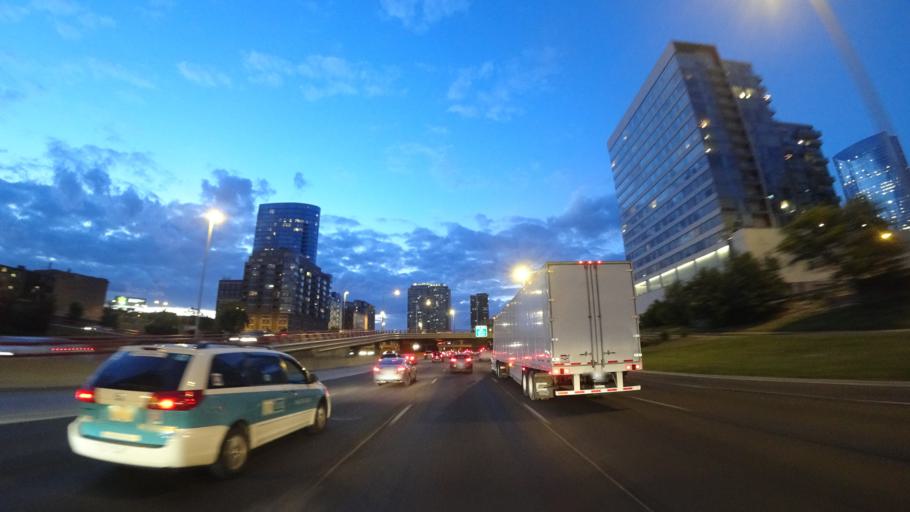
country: US
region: Illinois
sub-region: Cook County
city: Chicago
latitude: 41.8834
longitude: -87.6456
